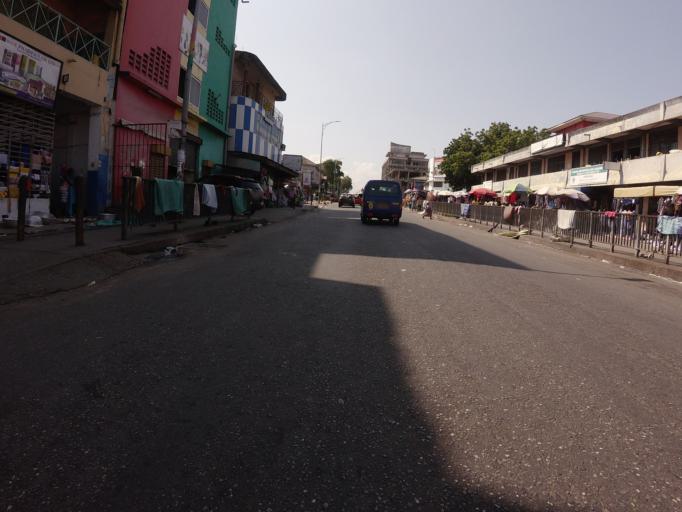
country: GH
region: Greater Accra
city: Accra
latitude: 5.5497
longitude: -0.2076
